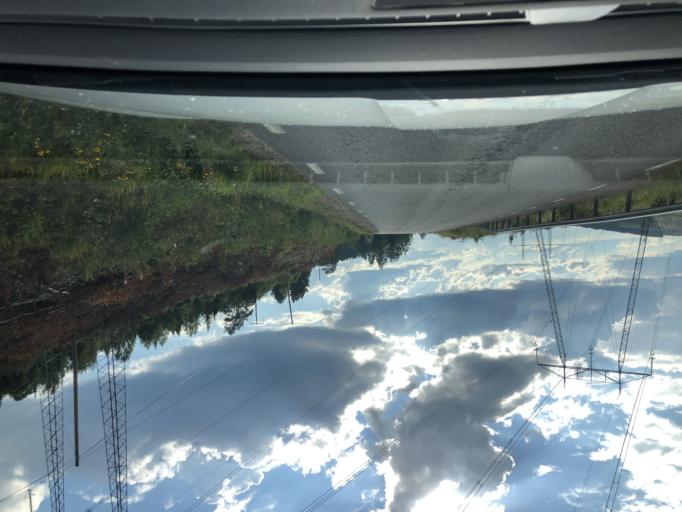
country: SE
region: Vaesternorrland
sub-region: Solleftea Kommun
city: Solleftea
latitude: 63.2099
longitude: 17.1687
